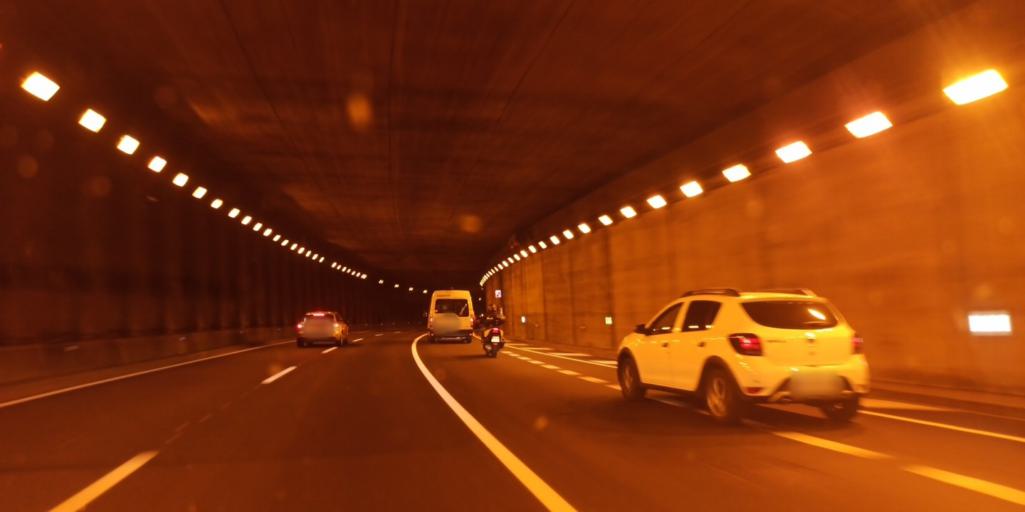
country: ES
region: Catalonia
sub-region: Provincia de Barcelona
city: les Corts
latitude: 41.3990
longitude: 2.1132
